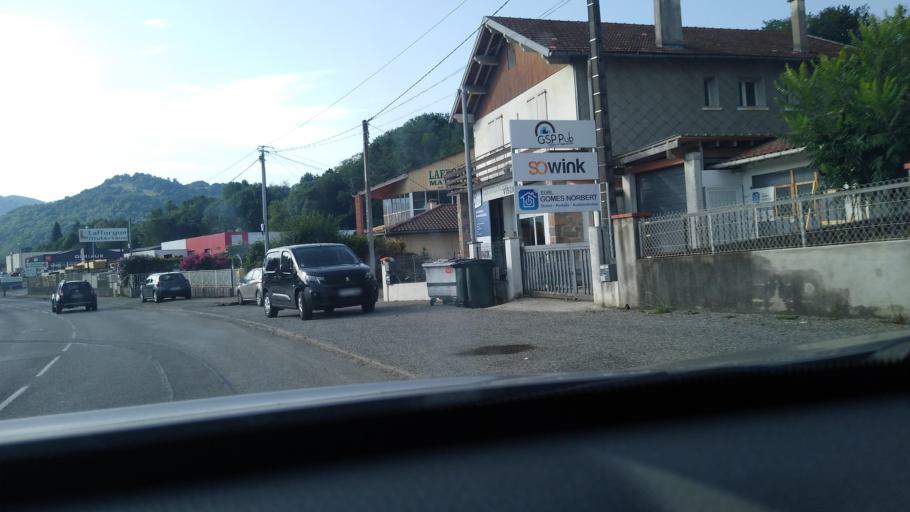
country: FR
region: Midi-Pyrenees
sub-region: Departement de l'Ariege
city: Saint-Girons
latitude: 42.9754
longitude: 1.1493
